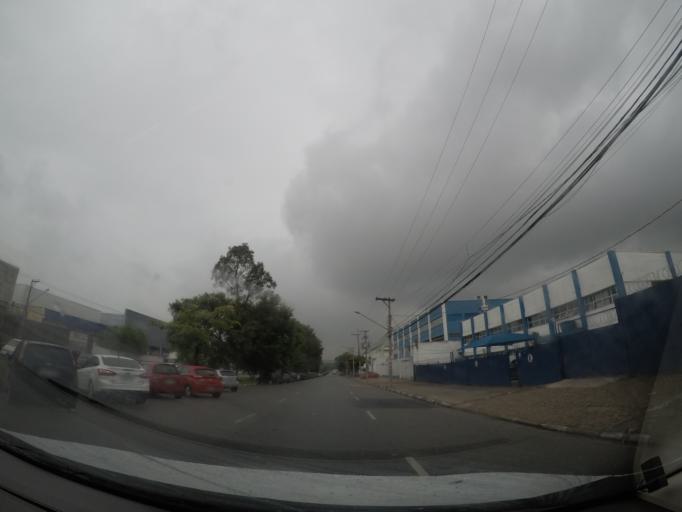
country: BR
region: Sao Paulo
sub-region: Guarulhos
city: Guarulhos
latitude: -23.4384
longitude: -46.5034
